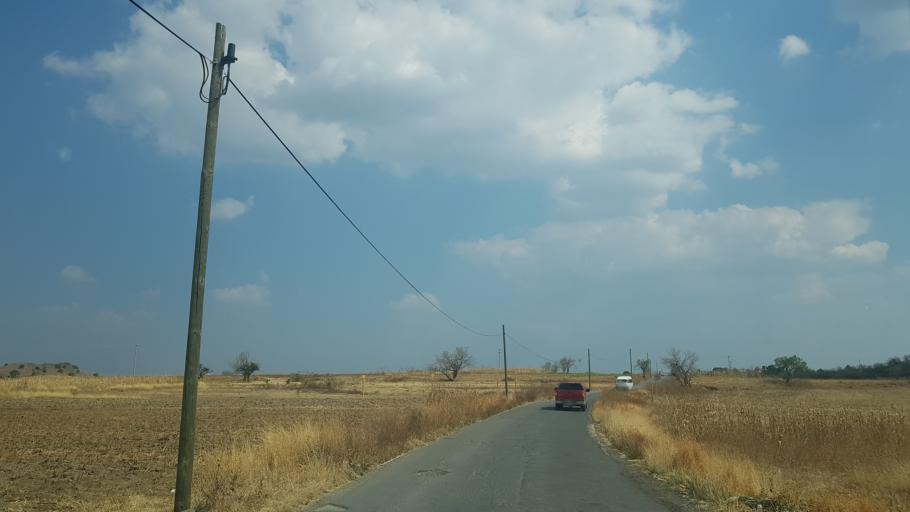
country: MX
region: Puebla
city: San Juan Amecac
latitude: 18.8205
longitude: -98.6533
